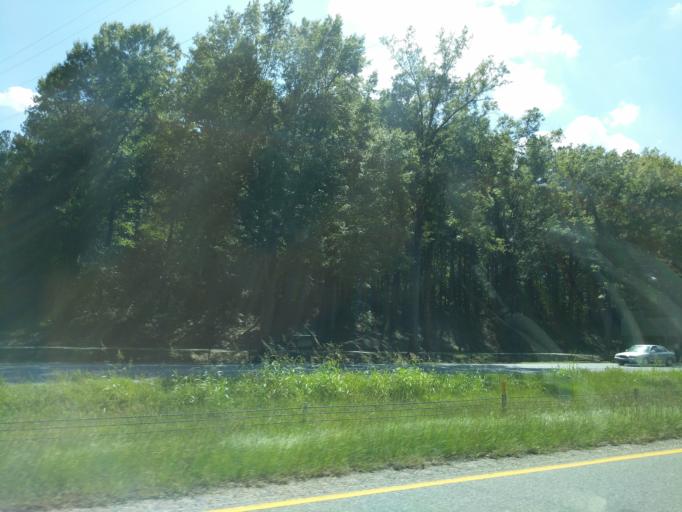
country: US
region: South Carolina
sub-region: Spartanburg County
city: Valley Falls
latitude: 34.9935
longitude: -81.9539
